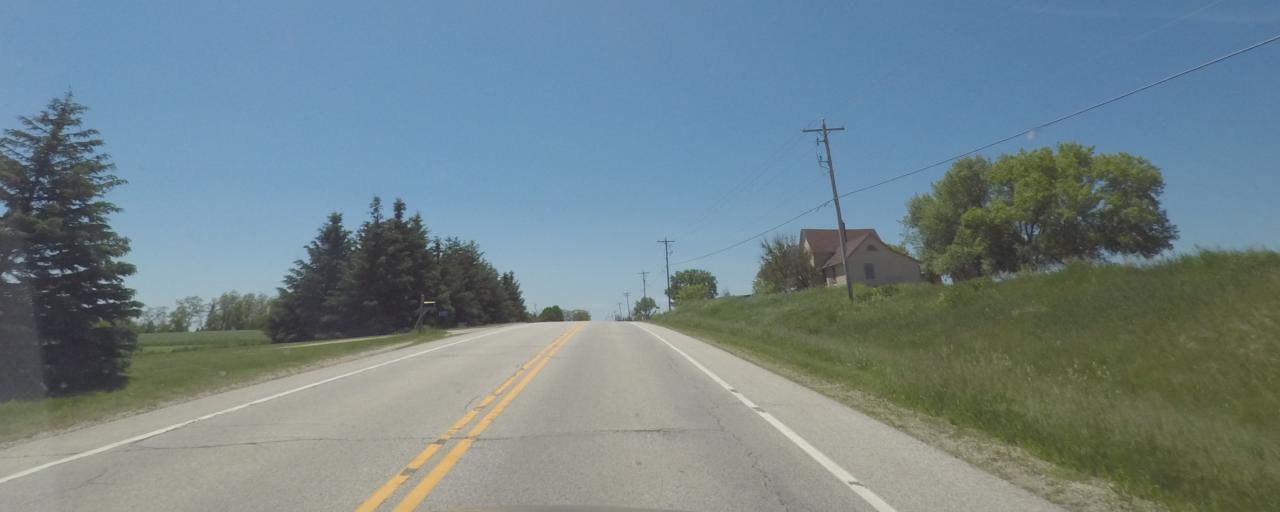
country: US
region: Wisconsin
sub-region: Ozaukee County
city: Kohler
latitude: 43.5819
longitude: -88.0540
